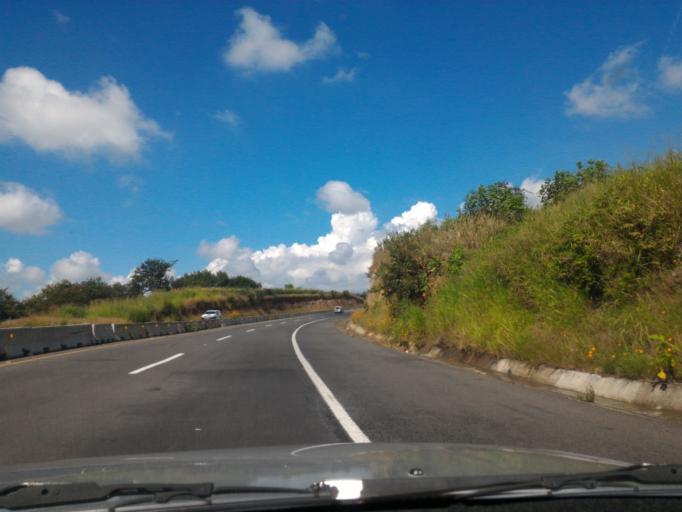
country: MX
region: Jalisco
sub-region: Tala
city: Los Ruisenores
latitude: 20.7411
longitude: -103.6349
